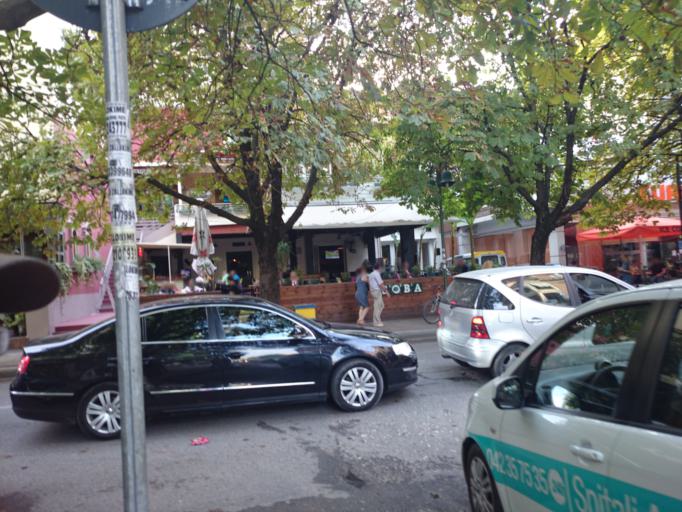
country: AL
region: Tirane
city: Tirana
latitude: 41.3217
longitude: 19.8137
